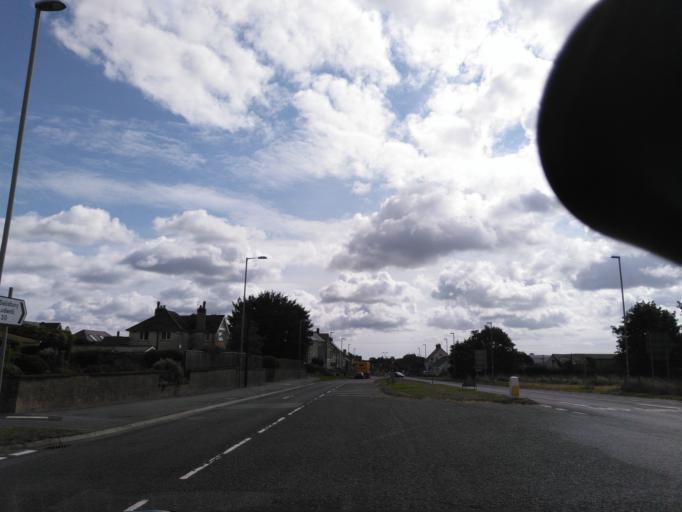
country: GB
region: England
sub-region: Dorset
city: Shaftesbury
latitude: 51.0018
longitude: -2.1819
